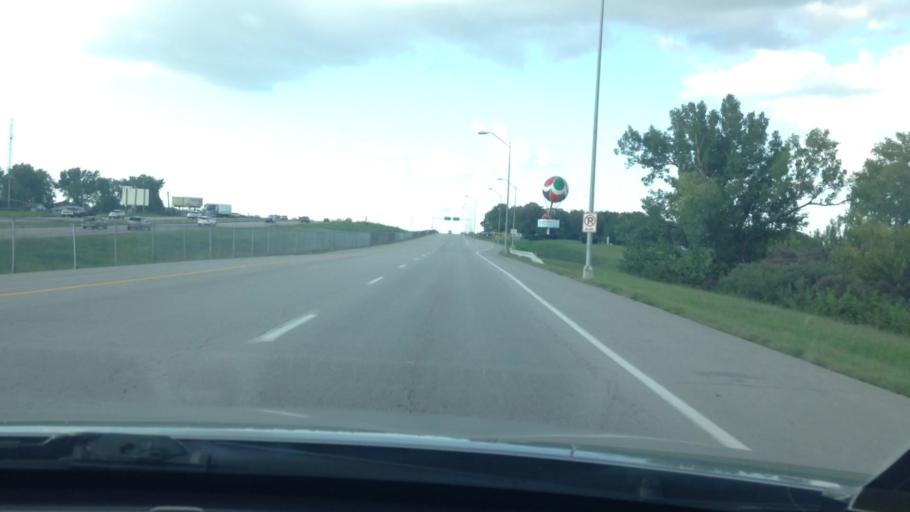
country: US
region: Missouri
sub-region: Clay County
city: Claycomo
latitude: 39.1744
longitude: -94.4920
